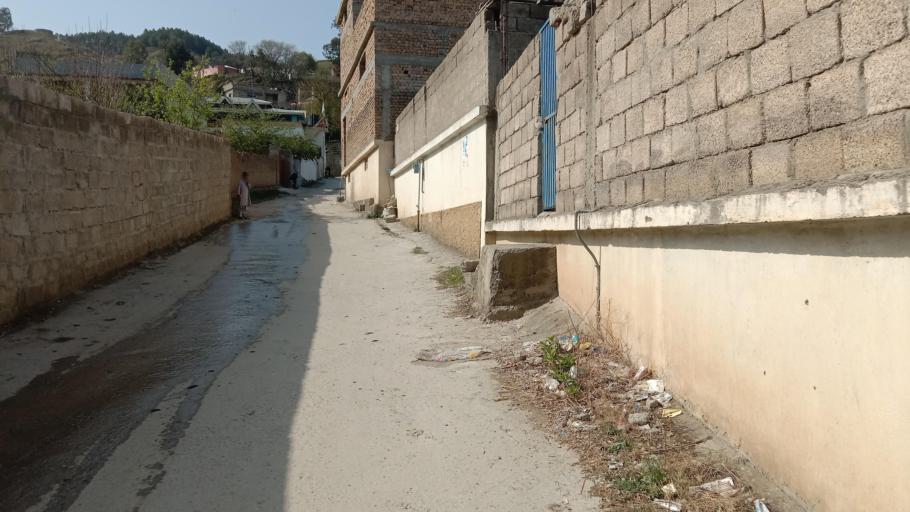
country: PK
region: Khyber Pakhtunkhwa
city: Abbottabad
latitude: 34.1763
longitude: 73.2125
